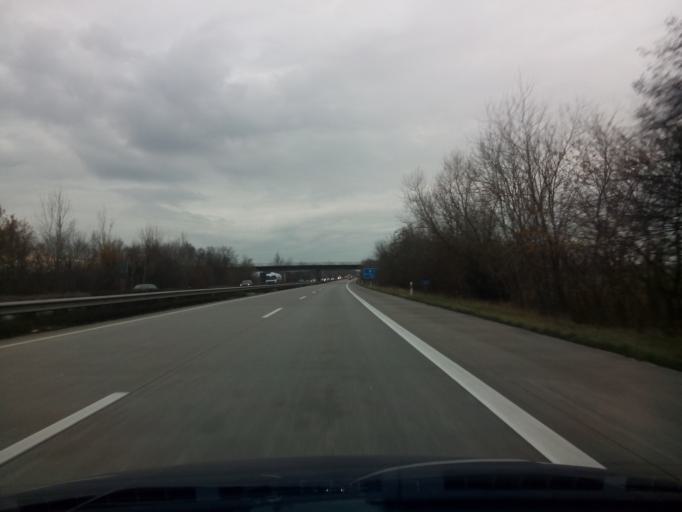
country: DE
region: Lower Saxony
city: Loxstedt
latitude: 53.4745
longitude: 8.6135
